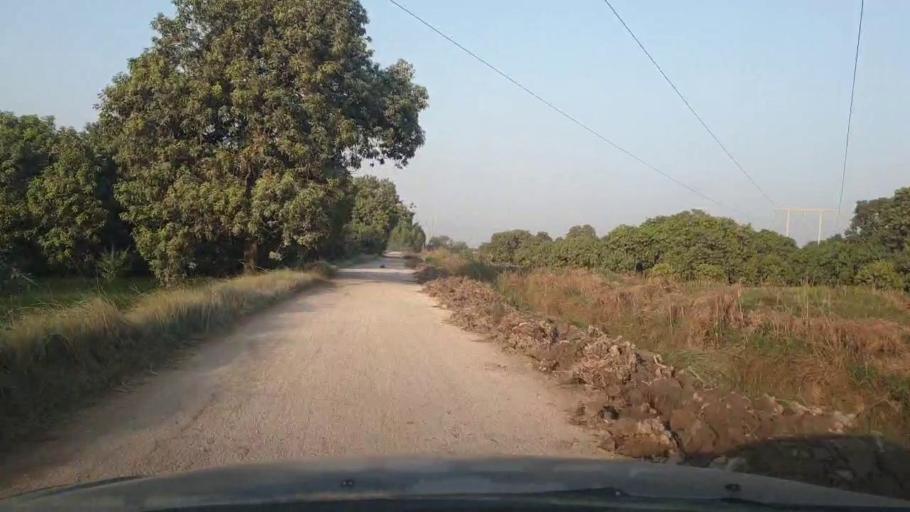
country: PK
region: Sindh
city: Tando Jam
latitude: 25.4250
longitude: 68.4951
